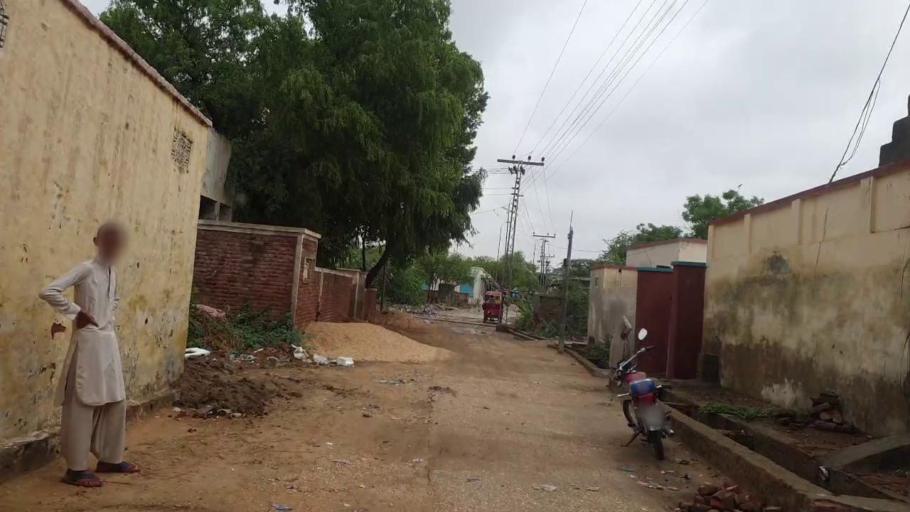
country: PK
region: Sindh
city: Diplo
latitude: 24.4641
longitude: 69.5815
